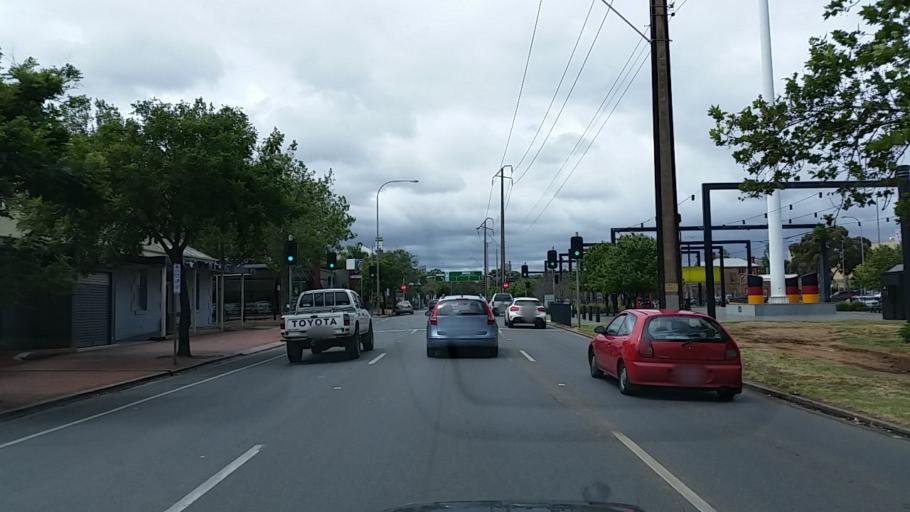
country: AU
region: South Australia
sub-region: City of West Torrens
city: Thebarton
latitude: -34.9066
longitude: 138.5744
